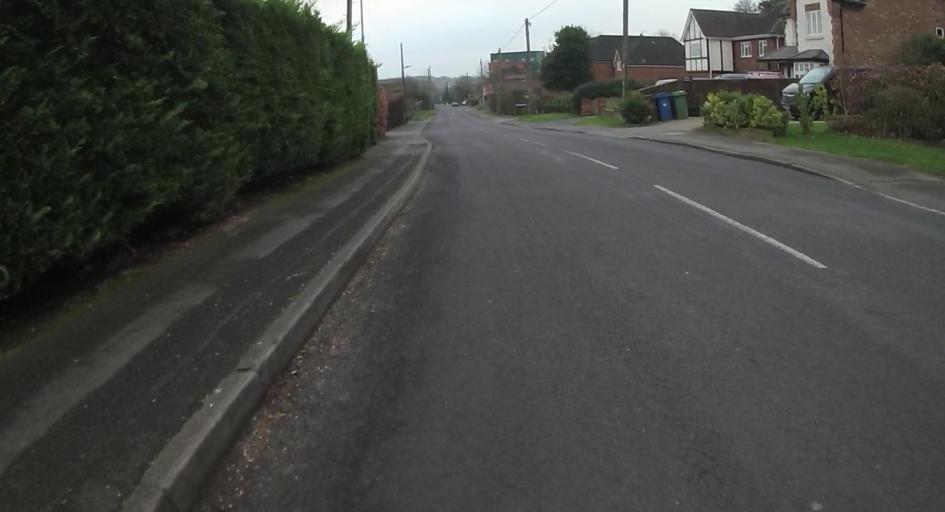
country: GB
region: England
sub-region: Bracknell Forest
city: Binfield
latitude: 51.4179
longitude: -0.7857
